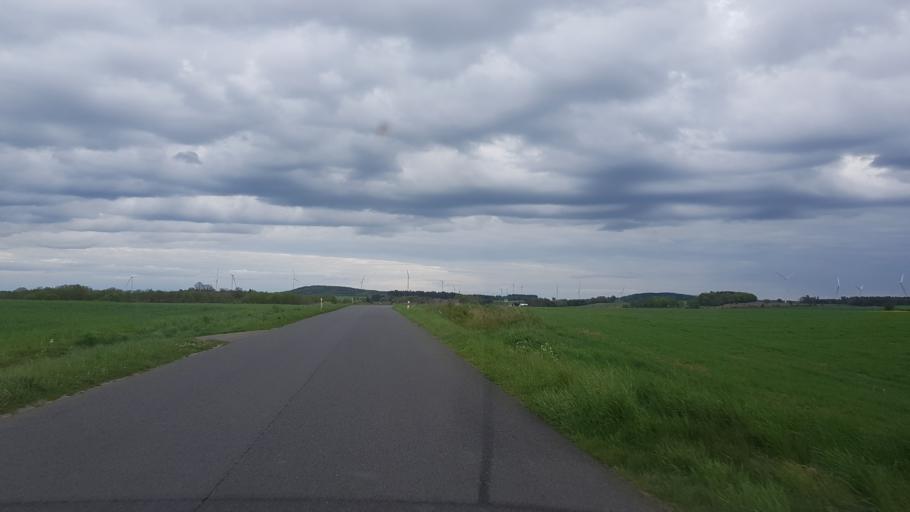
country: PL
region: West Pomeranian Voivodeship
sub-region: Powiat slawienski
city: Darlowo
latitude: 54.2789
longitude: 16.4997
